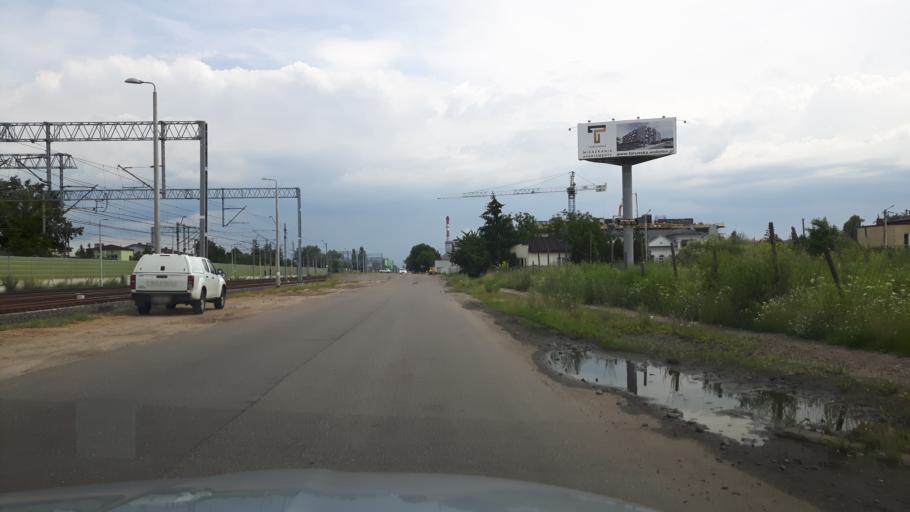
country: PL
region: Masovian Voivodeship
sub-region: Powiat wolominski
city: Wolomin
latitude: 52.3493
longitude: 21.2451
